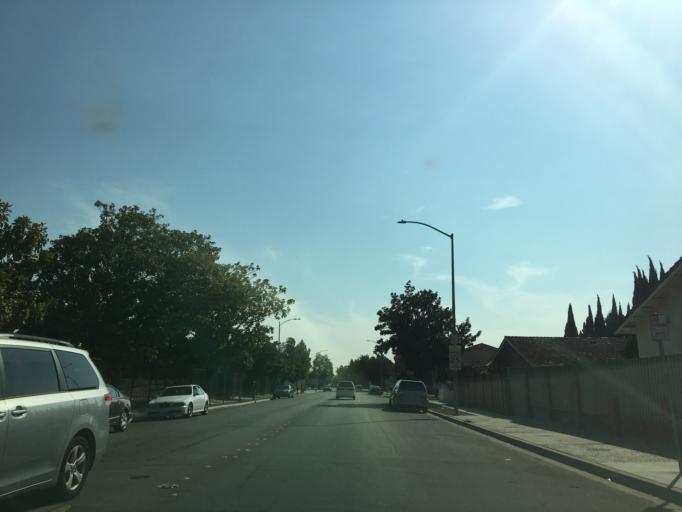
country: US
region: California
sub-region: Santa Clara County
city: Milpitas
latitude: 37.4491
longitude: -121.9047
